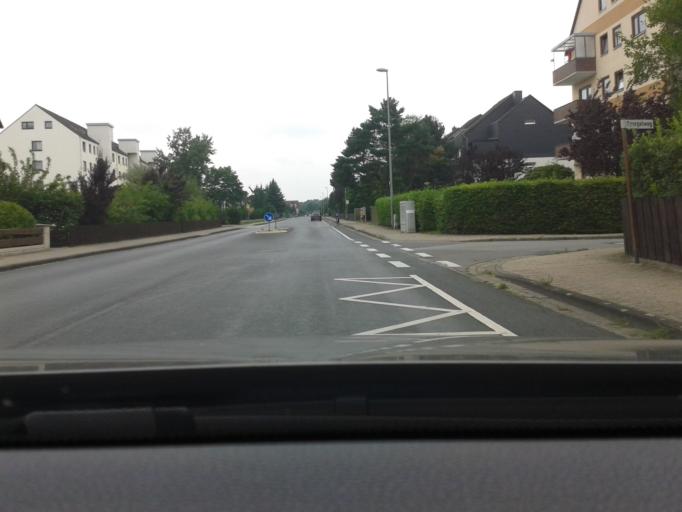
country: DE
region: Lower Saxony
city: Gifhorn
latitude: 52.4807
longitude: 10.5672
